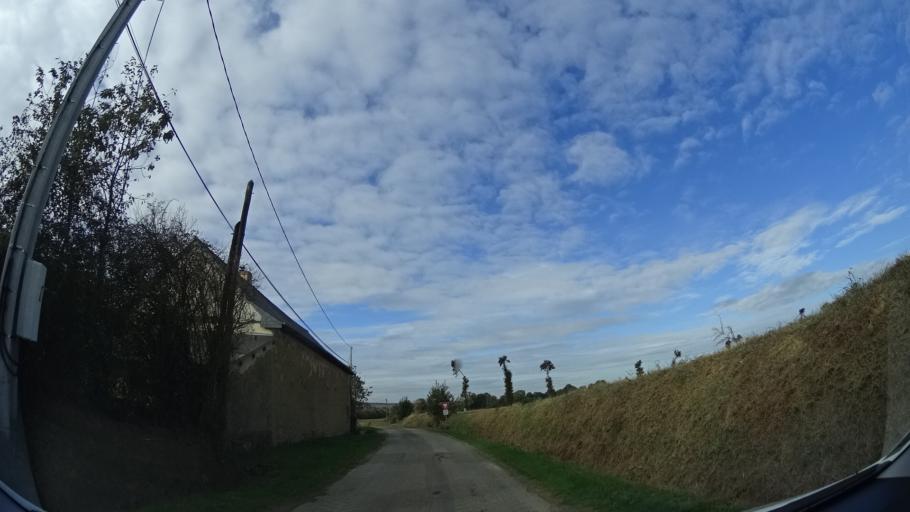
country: FR
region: Brittany
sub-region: Departement d'Ille-et-Vilaine
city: Vignoc
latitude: 48.2421
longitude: -1.8069
